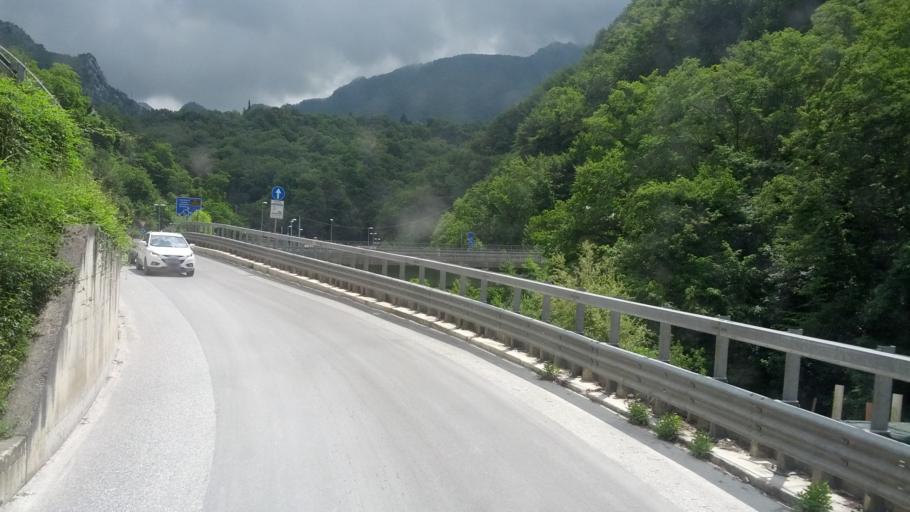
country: IT
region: Tuscany
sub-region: Provincia di Massa-Carrara
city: Carrara
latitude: 44.0821
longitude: 10.1130
